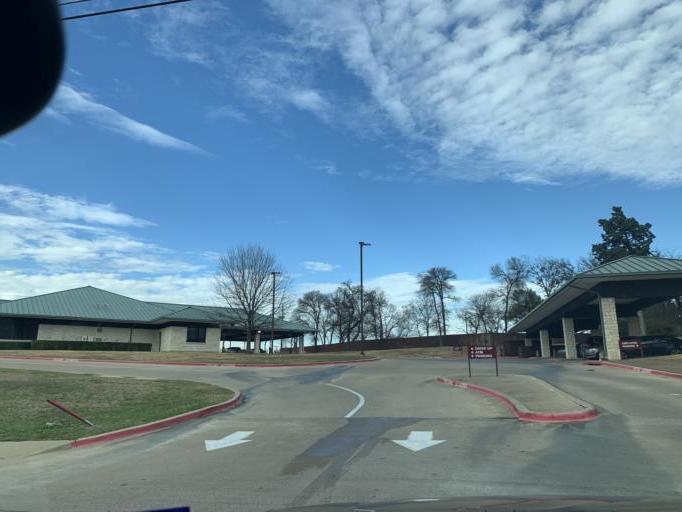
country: US
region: Texas
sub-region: Dallas County
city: Duncanville
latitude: 32.6329
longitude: -96.8977
